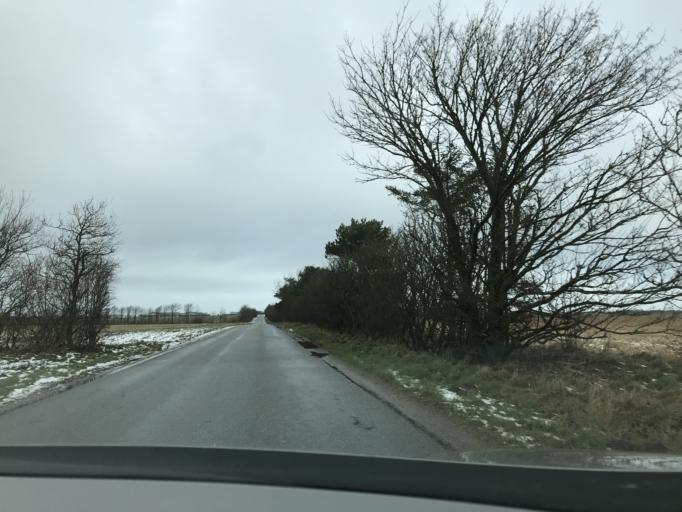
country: DK
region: South Denmark
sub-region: Varde Kommune
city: Varde
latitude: 55.6504
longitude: 8.4111
